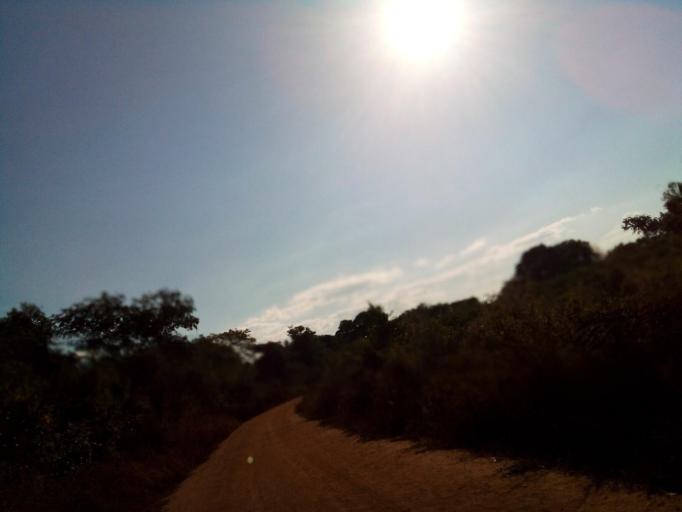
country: MZ
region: Zambezia
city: Quelimane
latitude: -17.4844
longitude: 36.5478
